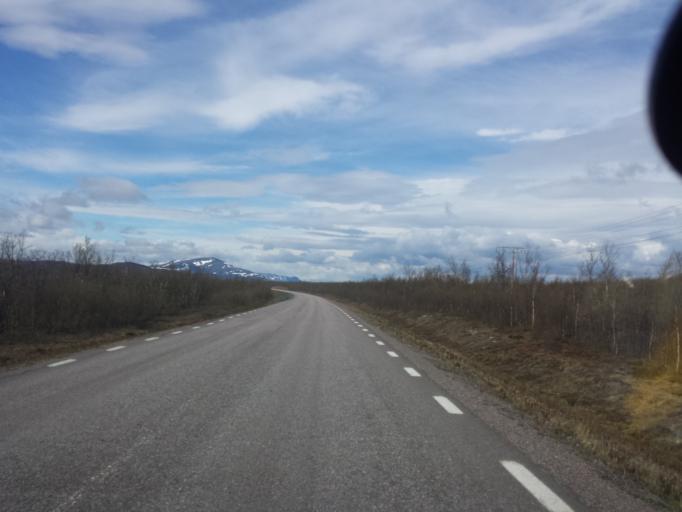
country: SE
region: Norrbotten
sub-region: Kiruna Kommun
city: Kiruna
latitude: 68.0496
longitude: 19.8304
